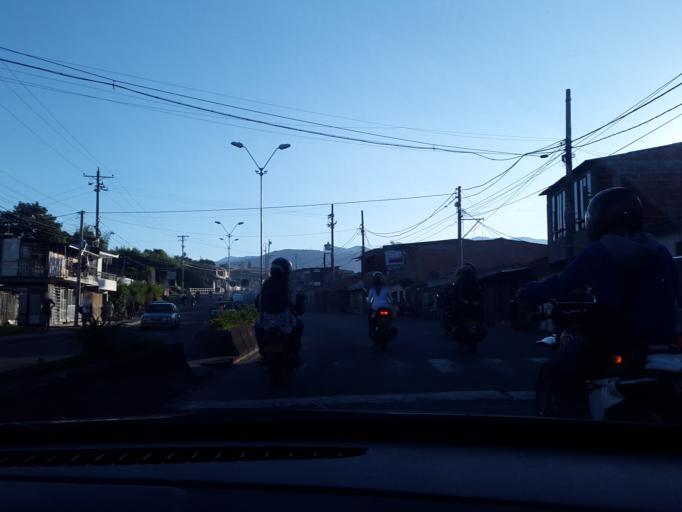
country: CO
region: Quindio
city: Armenia
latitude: 4.5315
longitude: -75.6885
